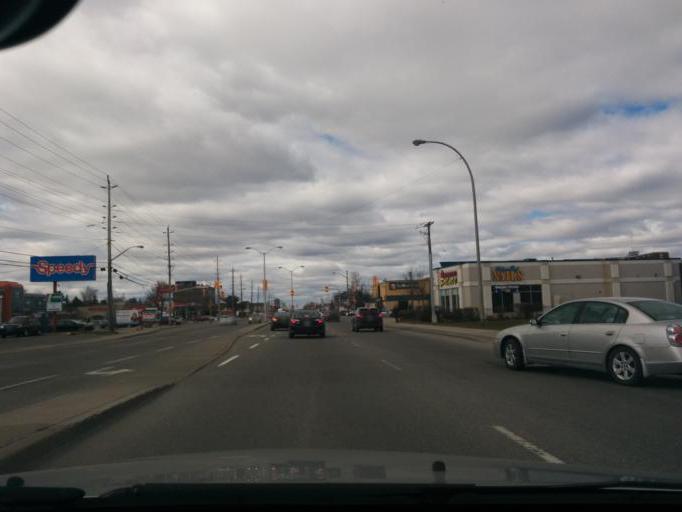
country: CA
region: Ontario
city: Ottawa
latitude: 45.3483
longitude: -75.7319
